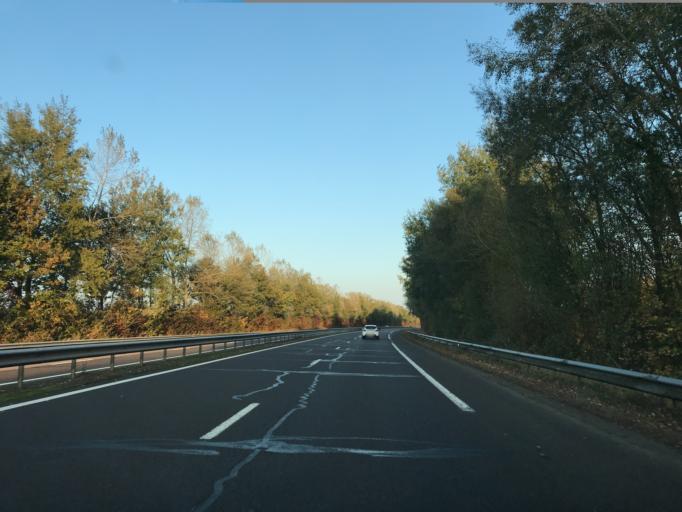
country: FR
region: Lower Normandy
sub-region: Departement de l'Orne
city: Mortagne-au-Perche
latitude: 48.5101
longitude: 0.3958
